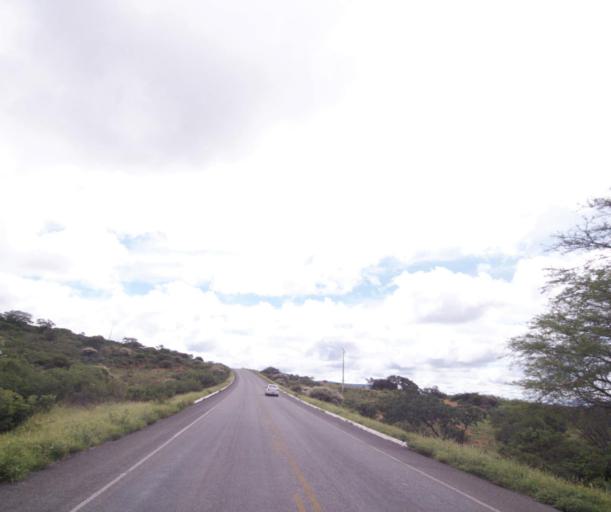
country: BR
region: Bahia
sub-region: Brumado
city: Brumado
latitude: -14.2182
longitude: -41.6605
